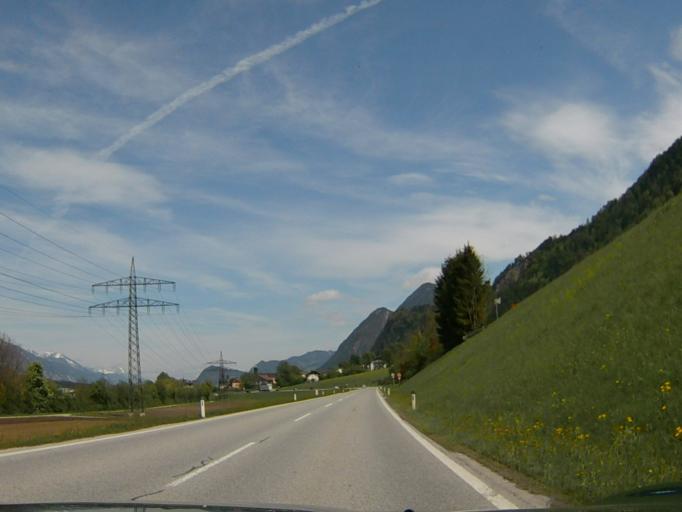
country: AT
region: Tyrol
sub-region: Politischer Bezirk Schwaz
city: Jenbach
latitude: 47.3875
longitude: 11.7891
